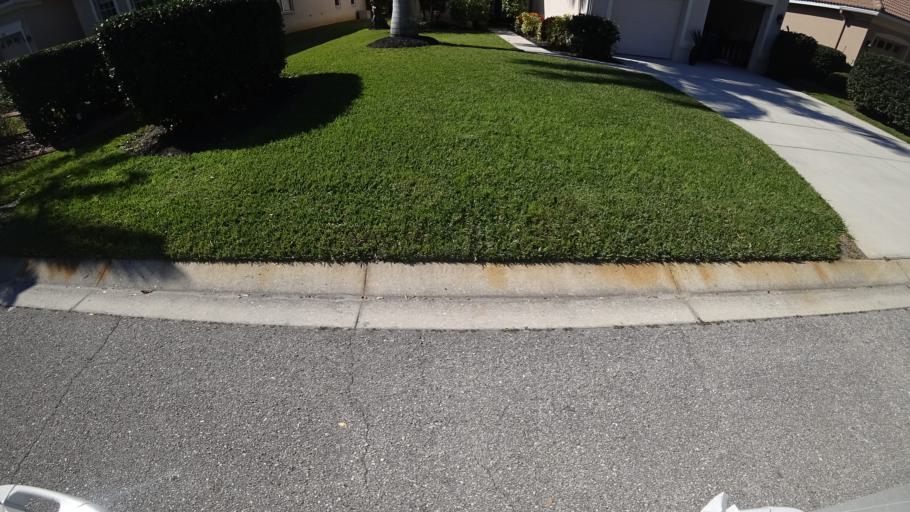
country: US
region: Florida
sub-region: Sarasota County
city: Desoto Lakes
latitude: 27.4212
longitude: -82.4606
